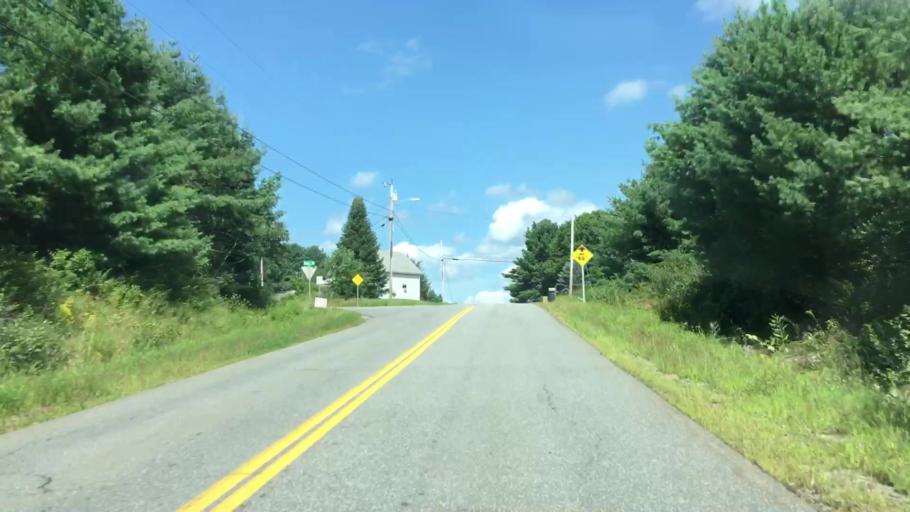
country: US
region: Maine
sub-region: Kennebec County
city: Manchester
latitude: 44.3543
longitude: -69.8163
